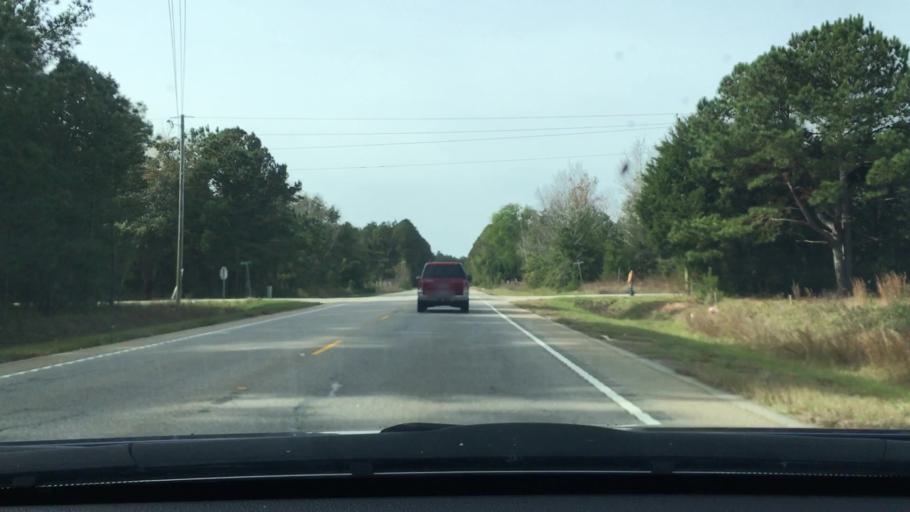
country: US
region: South Carolina
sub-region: Sumter County
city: Cherryvale
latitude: 33.9411
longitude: -80.4839
